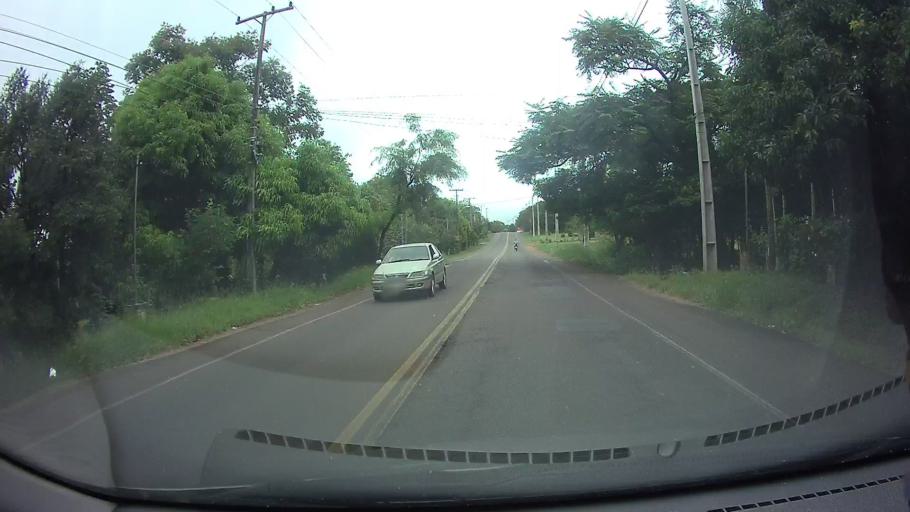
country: PY
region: Cordillera
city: Altos
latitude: -25.2875
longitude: -57.2650
